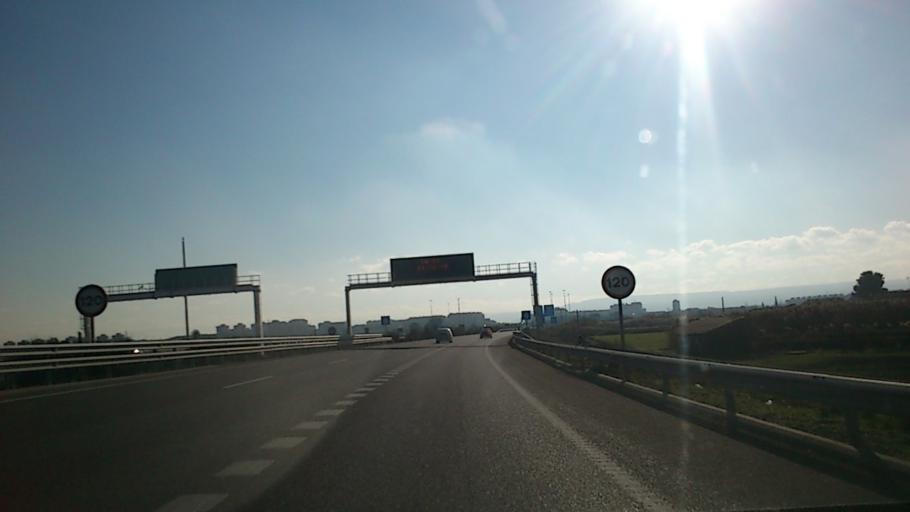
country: ES
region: Aragon
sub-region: Provincia de Zaragoza
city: Zaragoza
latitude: 41.6859
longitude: -0.8329
